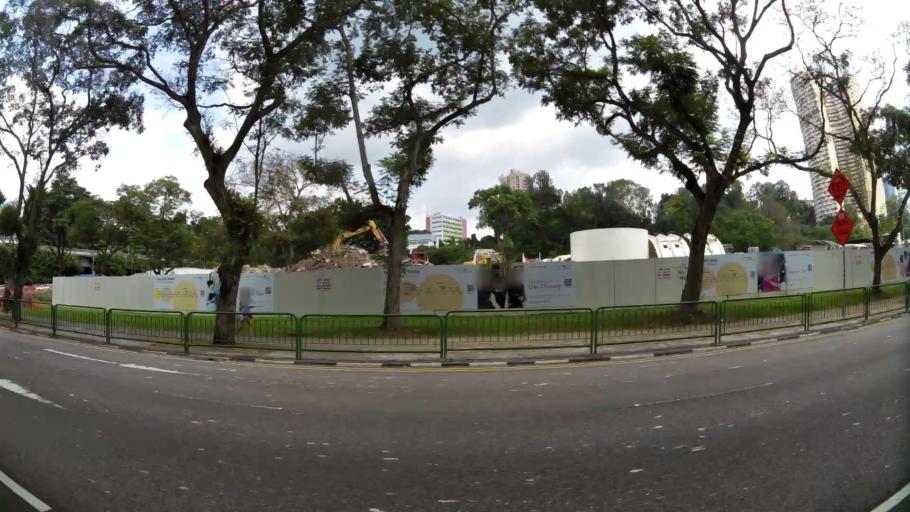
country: SG
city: Singapore
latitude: 1.2826
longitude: 103.8370
